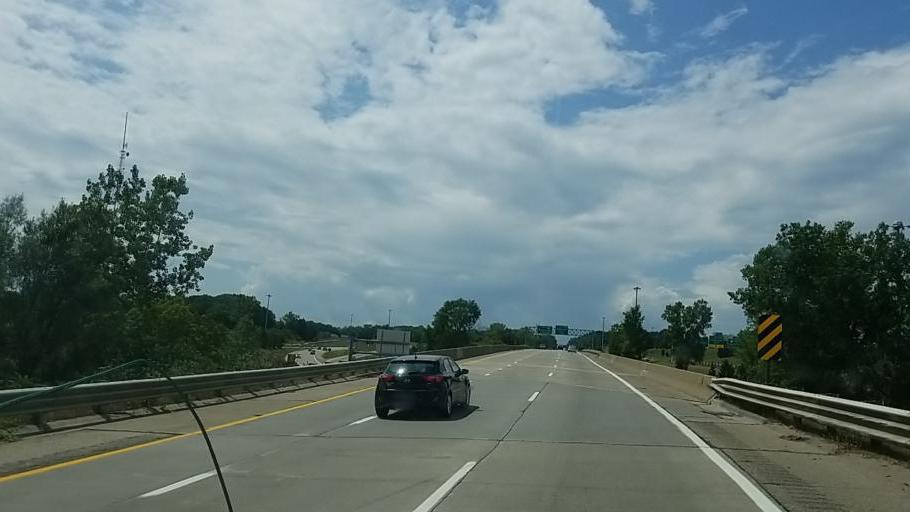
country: US
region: Michigan
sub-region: Kent County
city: Comstock Park
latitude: 43.0161
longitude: -85.6800
